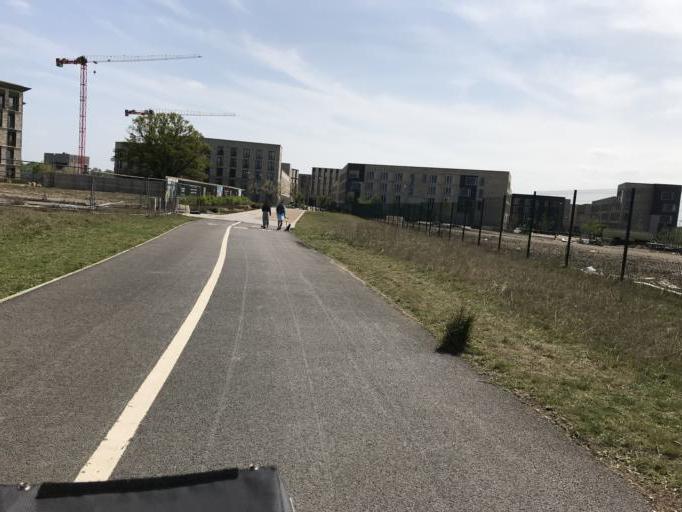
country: GB
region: England
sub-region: Cambridgeshire
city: Girton
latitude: 52.2210
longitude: 0.0848
